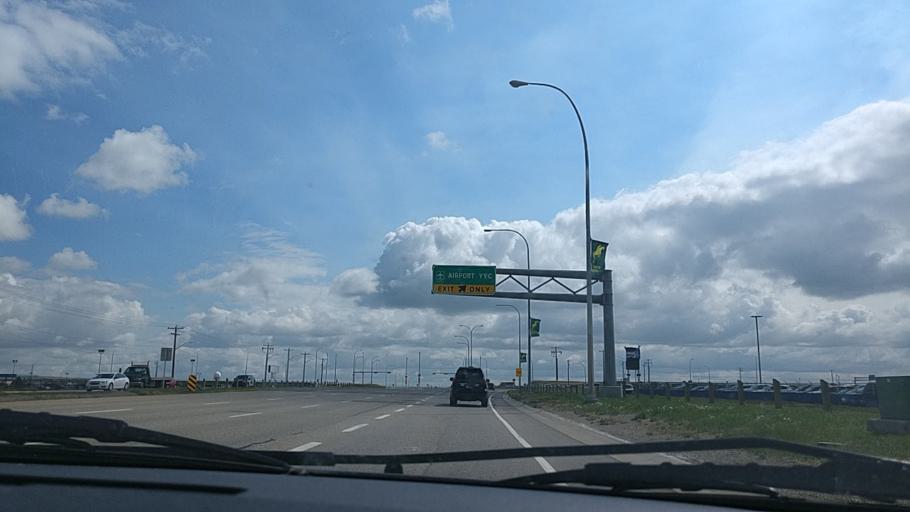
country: CA
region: Alberta
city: Calgary
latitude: 51.1394
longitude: -114.0063
